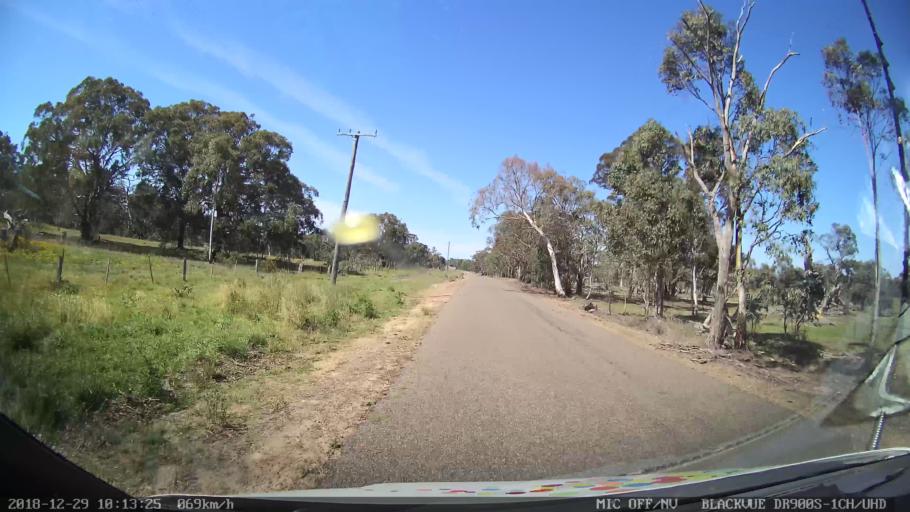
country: AU
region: New South Wales
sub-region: Yass Valley
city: Gundaroo
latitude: -34.9030
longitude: 149.4441
